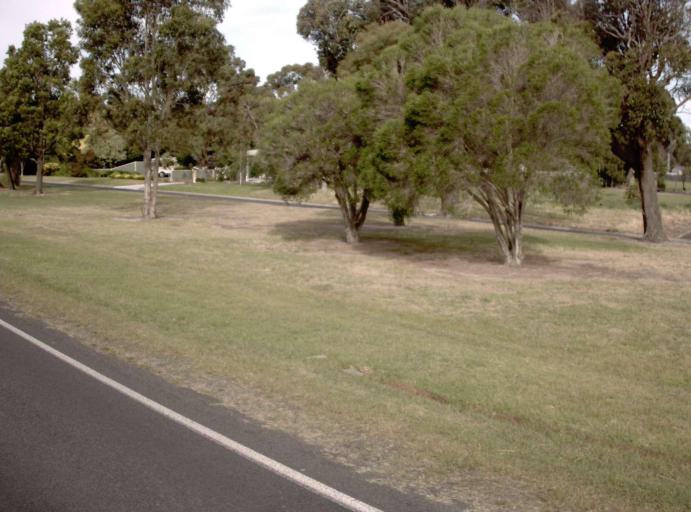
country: AU
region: Victoria
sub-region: Latrobe
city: Traralgon
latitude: -38.1271
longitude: 146.5659
